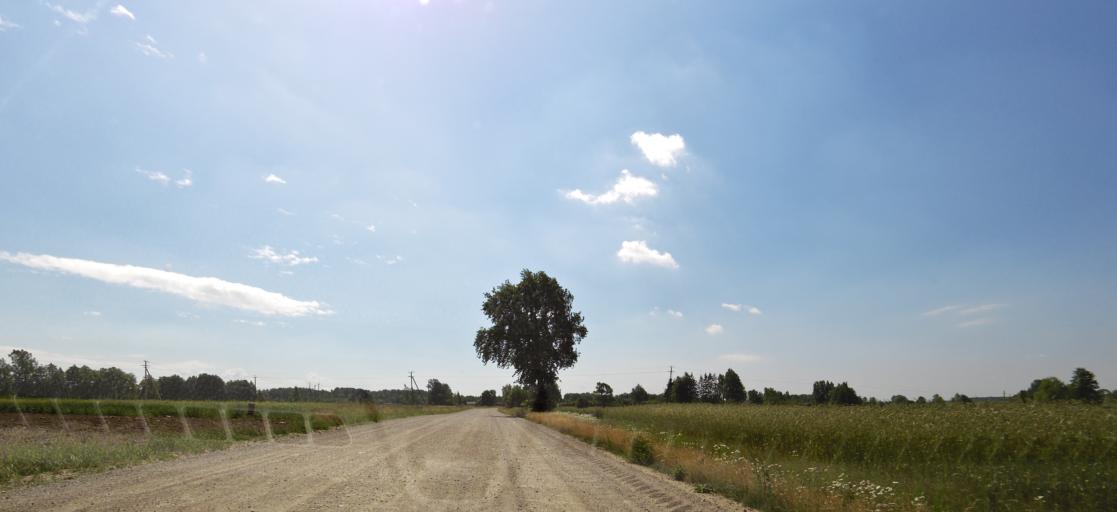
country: LT
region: Panevezys
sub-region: Birzai
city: Birzai
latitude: 56.1917
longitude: 24.9320
